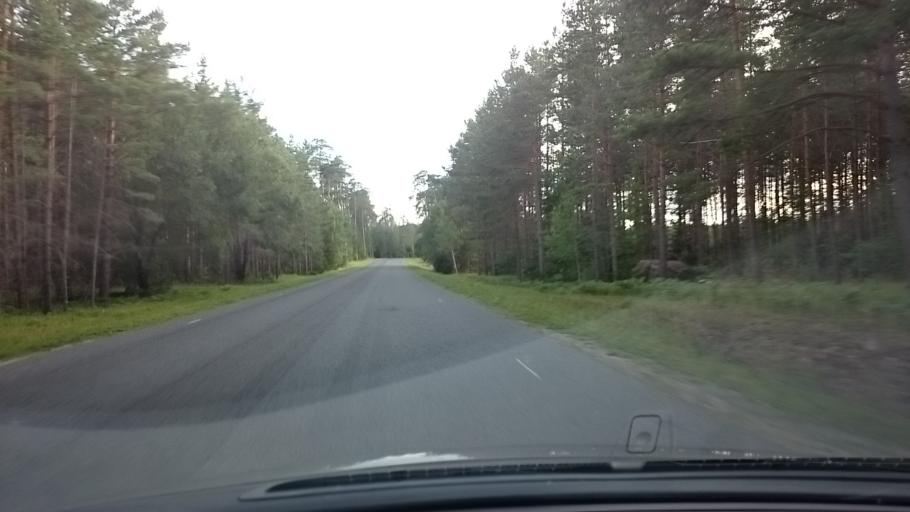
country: EE
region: Saare
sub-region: Kuressaare linn
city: Kuressaare
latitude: 58.4223
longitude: 22.1741
